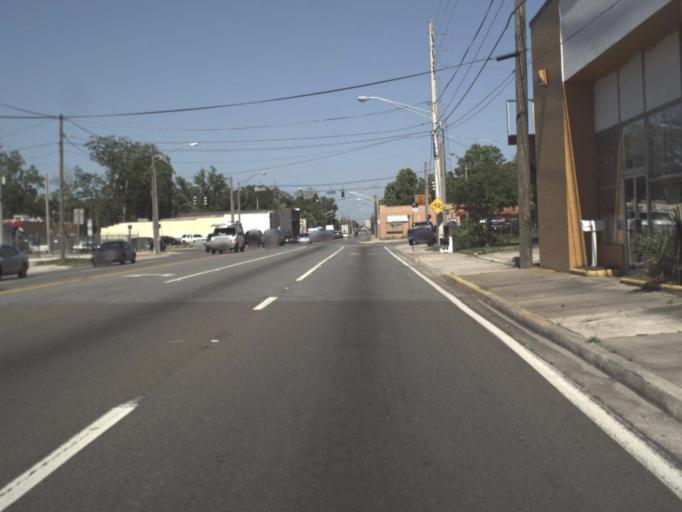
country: US
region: Florida
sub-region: Duval County
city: Jacksonville
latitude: 30.3314
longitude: -81.7067
